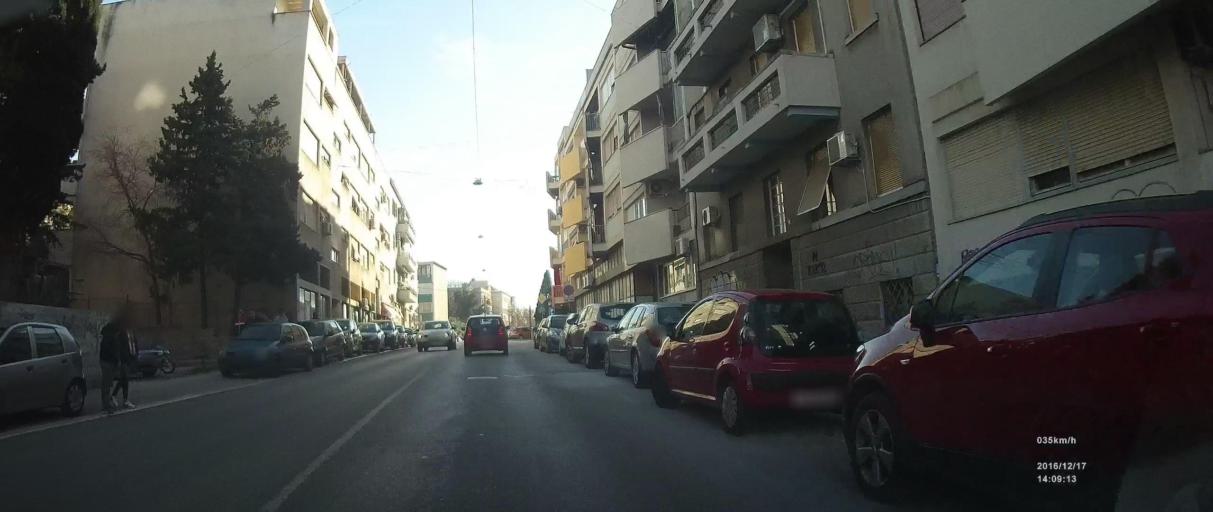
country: HR
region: Splitsko-Dalmatinska
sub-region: Grad Split
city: Split
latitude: 43.5173
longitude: 16.4348
